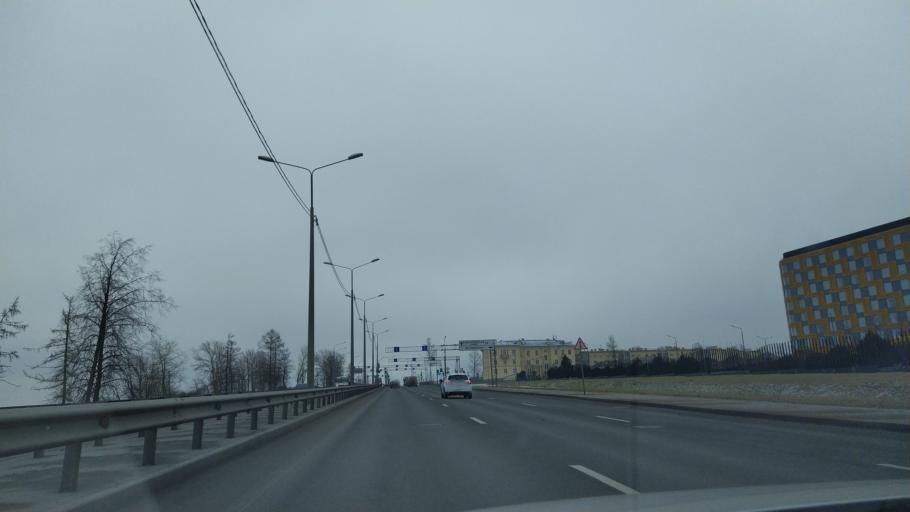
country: RU
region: St.-Petersburg
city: Aleksandrovskaya
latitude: 59.7644
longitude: 30.3581
